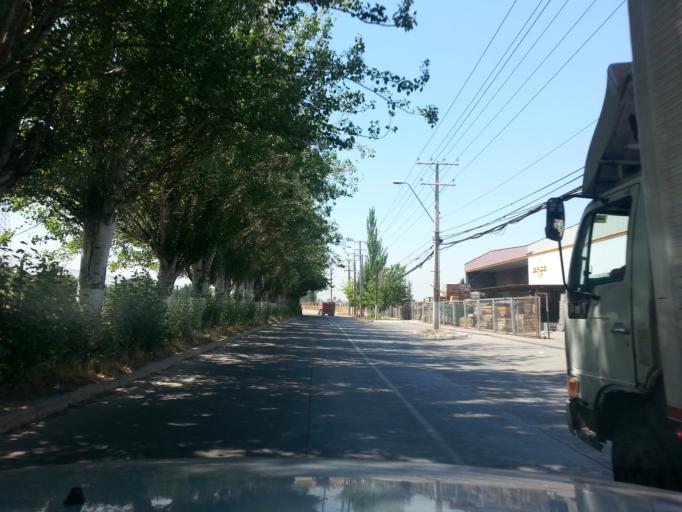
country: CL
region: Santiago Metropolitan
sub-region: Provincia de Chacabuco
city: Chicureo Abajo
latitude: -33.3557
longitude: -70.6926
